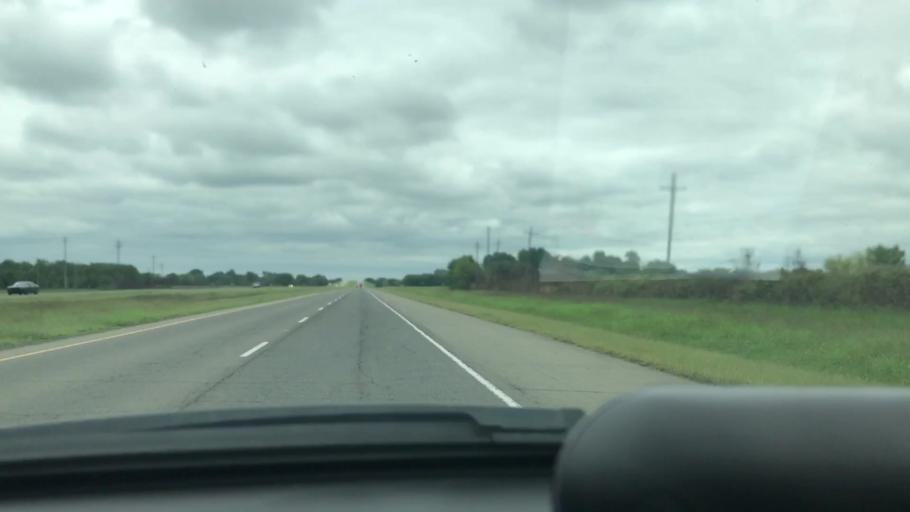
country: US
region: Oklahoma
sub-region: Wagoner County
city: Wagoner
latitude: 35.8653
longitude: -95.4026
